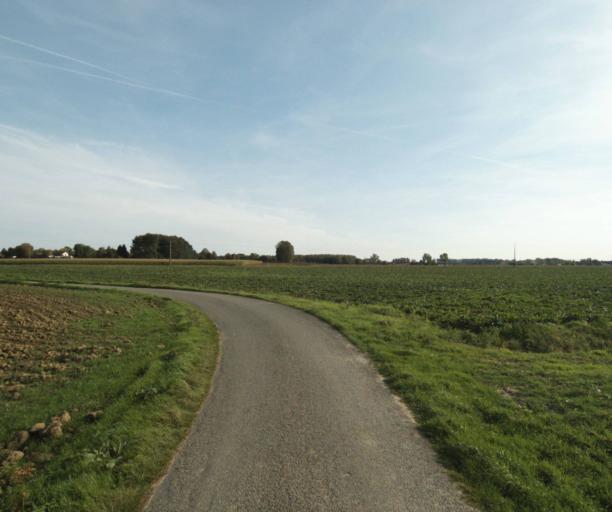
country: FR
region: Nord-Pas-de-Calais
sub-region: Departement du Nord
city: Fournes-en-Weppes
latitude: 50.5863
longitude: 2.8755
